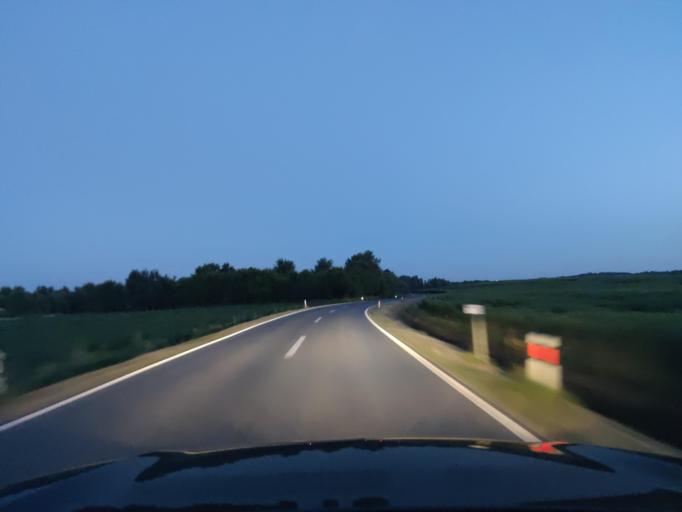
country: HR
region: Medimurska
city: Vratisinec
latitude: 46.4911
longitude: 16.4261
